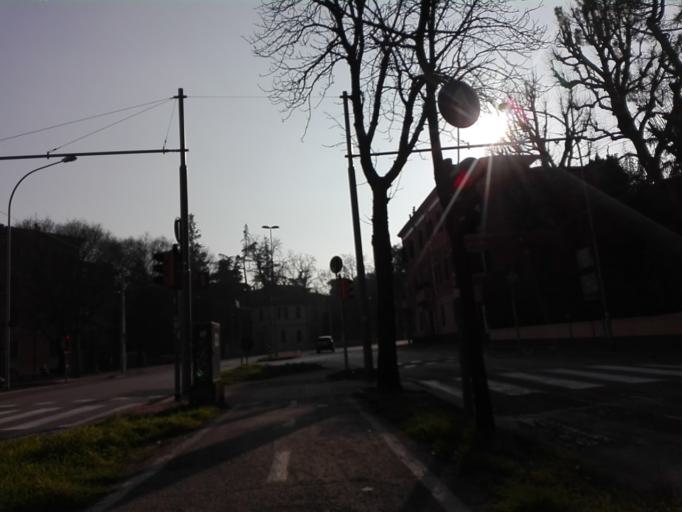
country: IT
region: Emilia-Romagna
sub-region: Provincia di Bologna
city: Bologna
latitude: 44.4864
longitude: 11.3580
